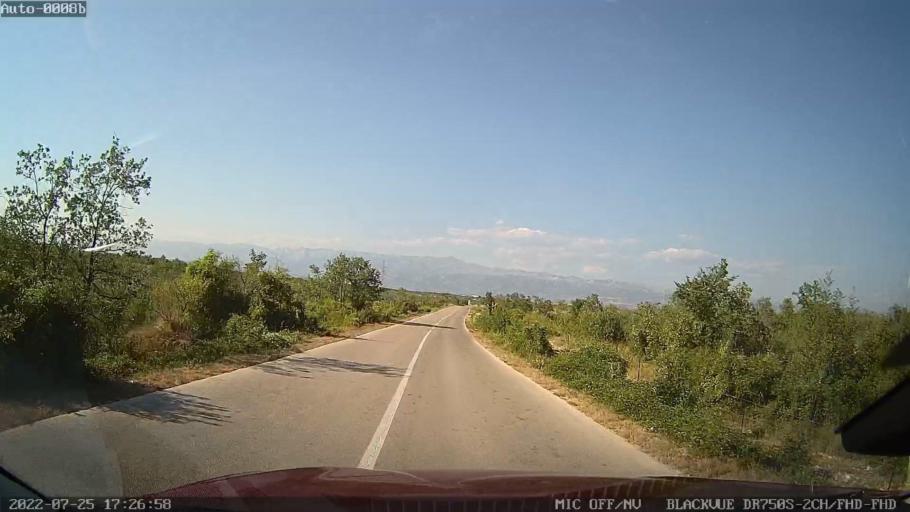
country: HR
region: Zadarska
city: Pridraga
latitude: 44.1386
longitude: 15.5028
